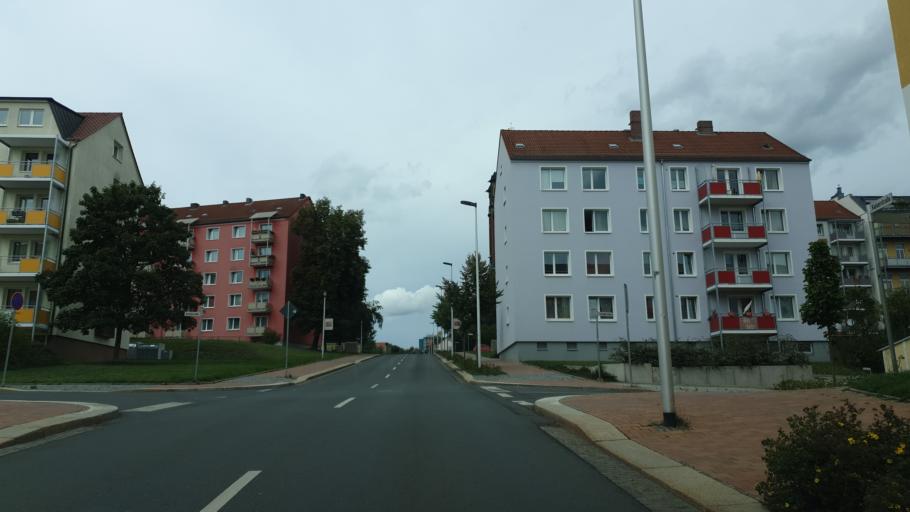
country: DE
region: Saxony
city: Plauen
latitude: 50.5012
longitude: 12.1408
